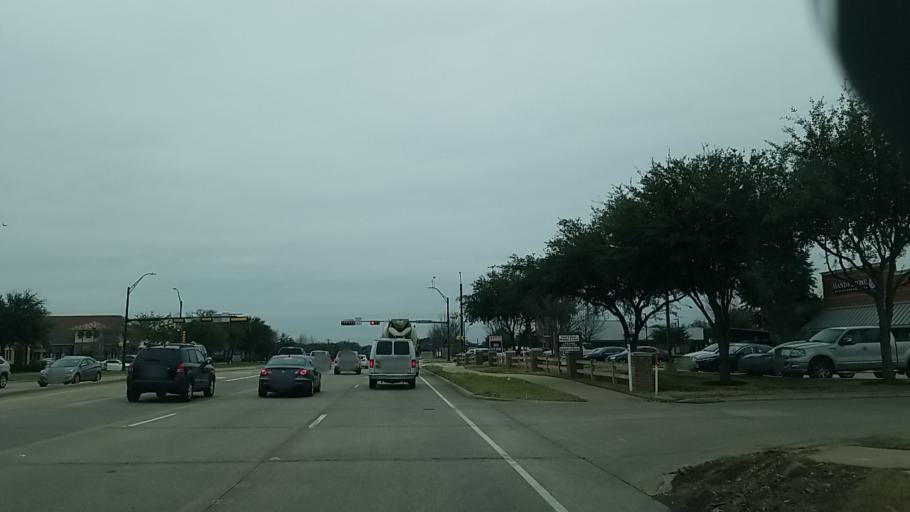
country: US
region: Texas
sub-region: Denton County
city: Flower Mound
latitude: 33.0344
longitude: -97.0708
